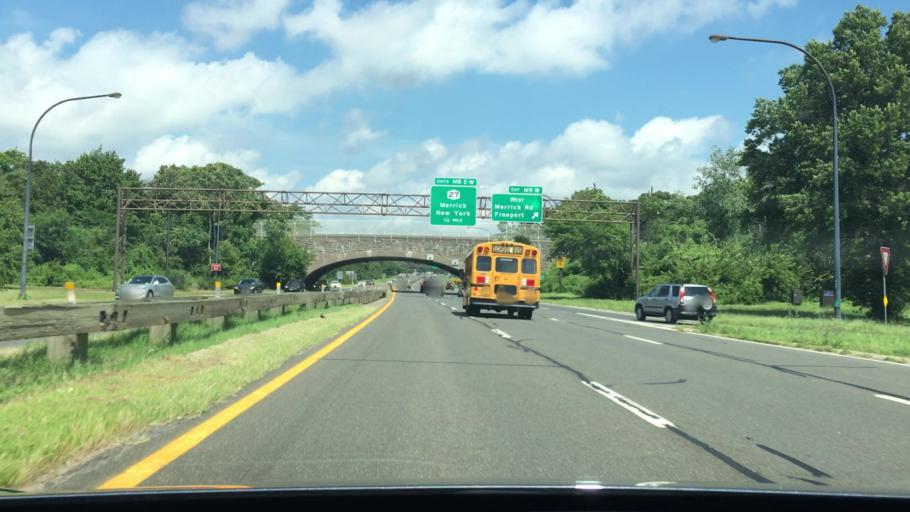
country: US
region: New York
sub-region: Nassau County
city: Freeport
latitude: 40.6528
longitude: -73.5666
